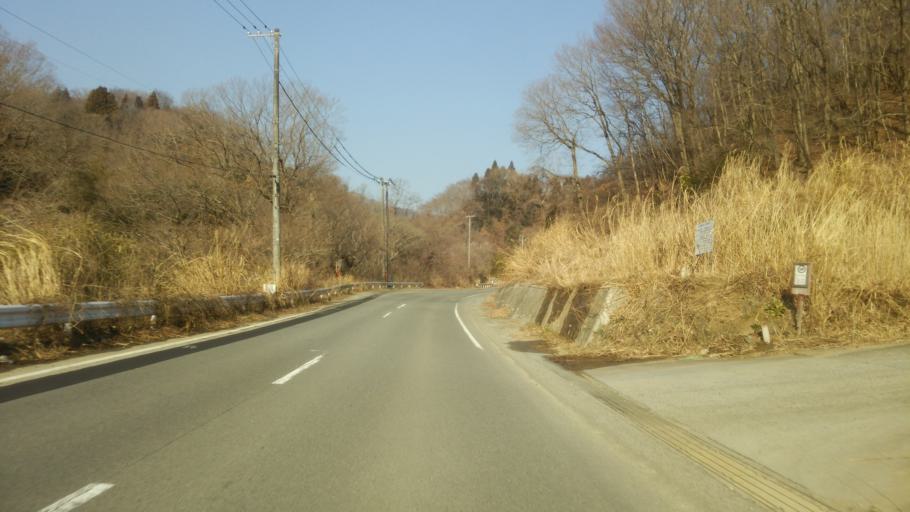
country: JP
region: Fukushima
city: Iwaki
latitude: 37.0364
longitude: 140.8112
